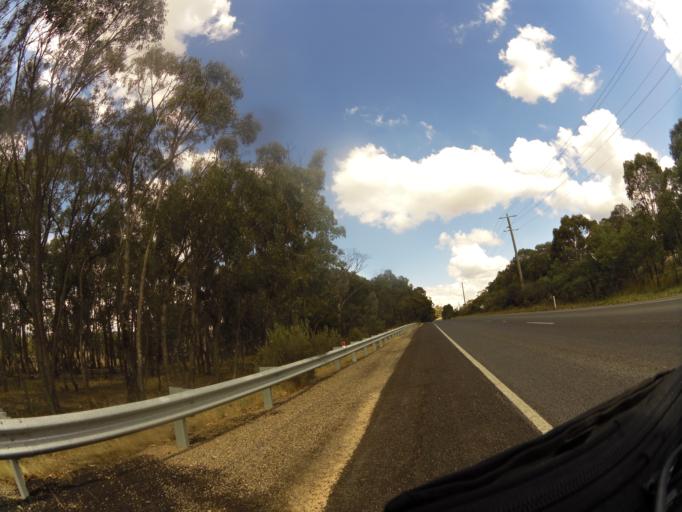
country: AU
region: Victoria
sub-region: Benalla
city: Benalla
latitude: -36.7866
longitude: 146.0104
